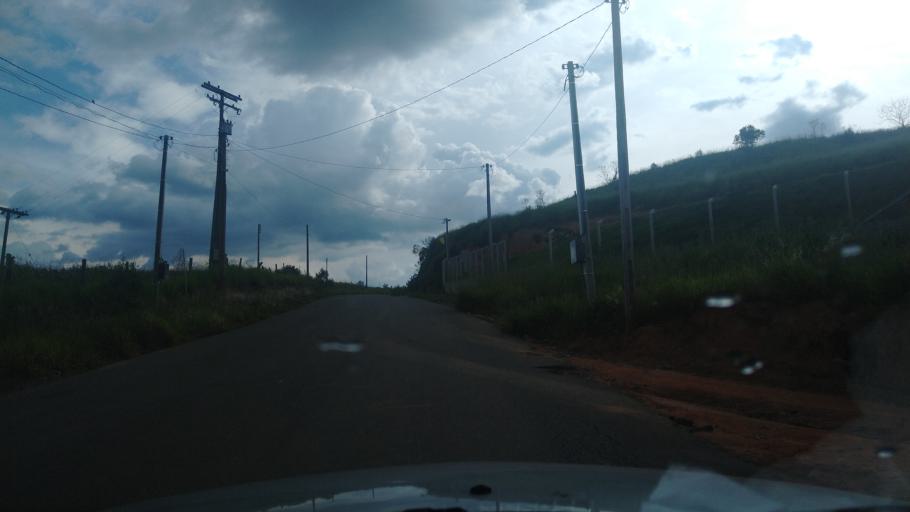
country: BR
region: Minas Gerais
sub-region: Extrema
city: Extrema
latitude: -22.7349
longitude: -46.3659
